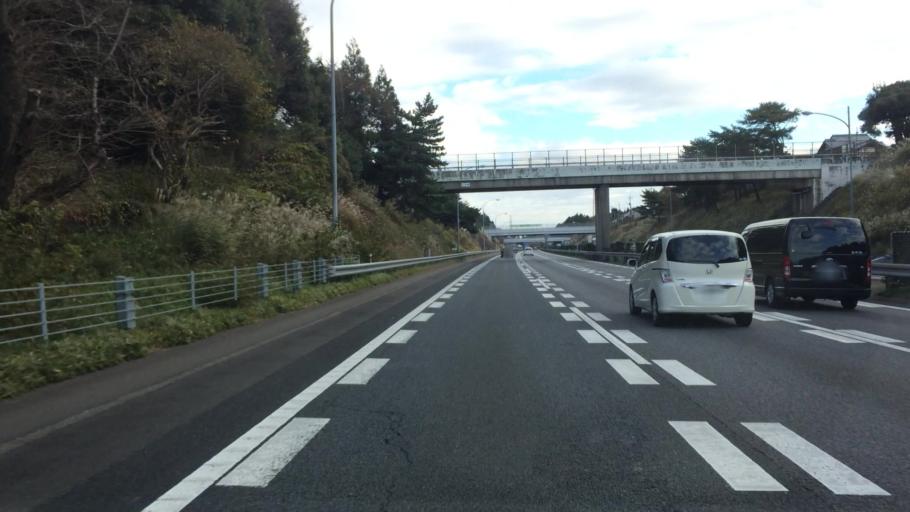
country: JP
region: Chiba
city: Shisui
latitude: 35.7002
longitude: 140.2641
